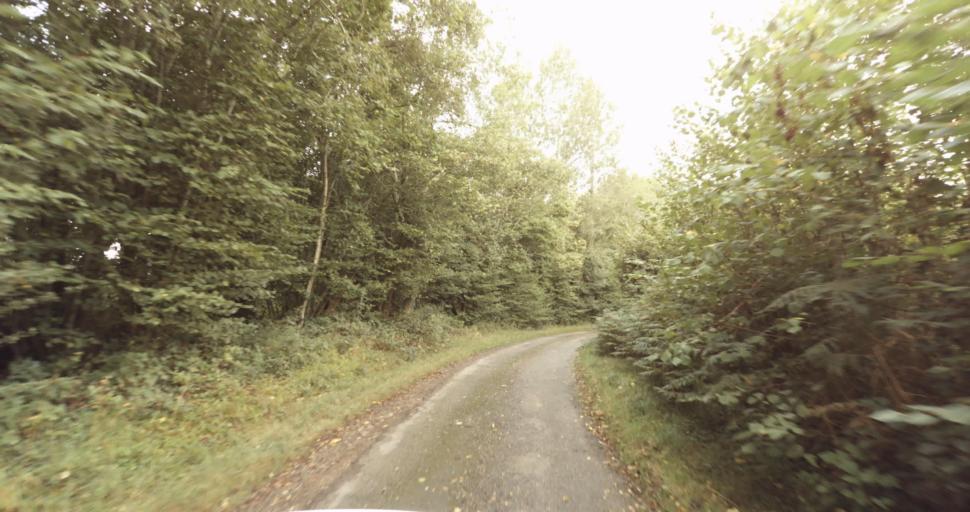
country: FR
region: Lower Normandy
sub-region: Departement de l'Orne
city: Trun
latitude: 48.9040
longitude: 0.1042
